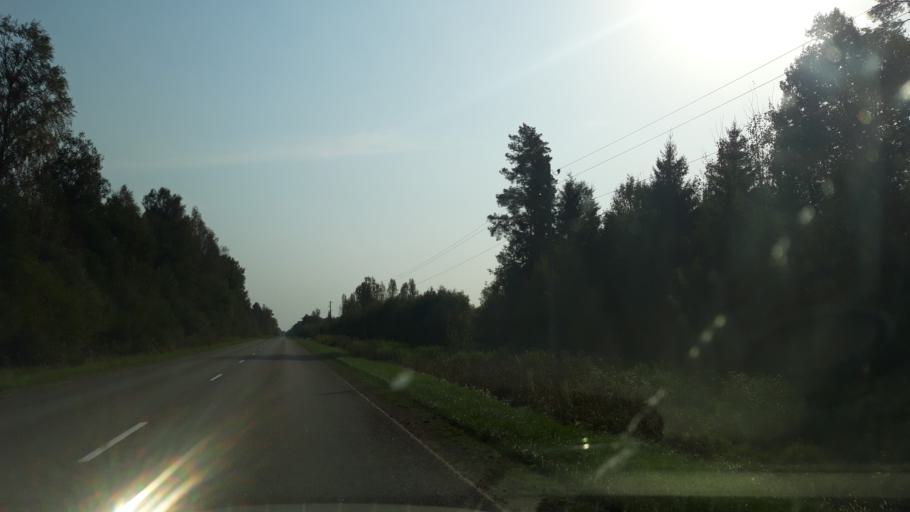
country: LV
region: Burtnieki
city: Matisi
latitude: 57.6498
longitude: 25.2377
